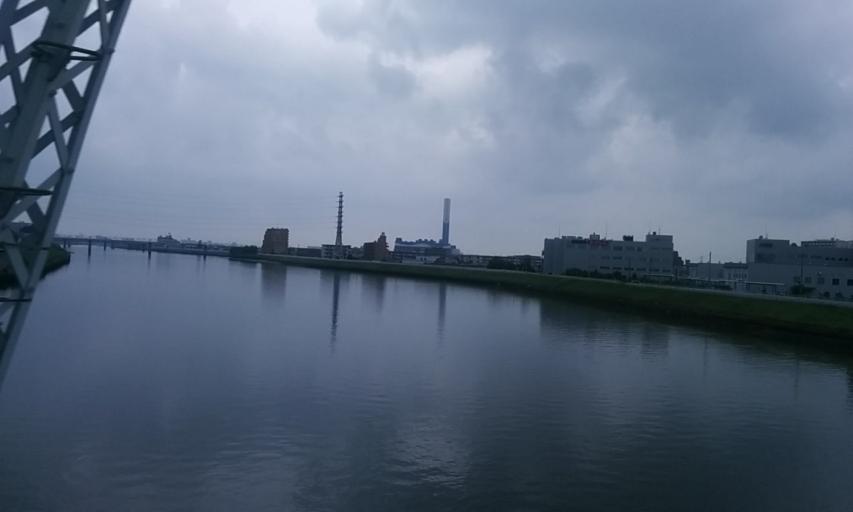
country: JP
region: Chiba
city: Matsudo
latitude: 35.7682
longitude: 139.8587
